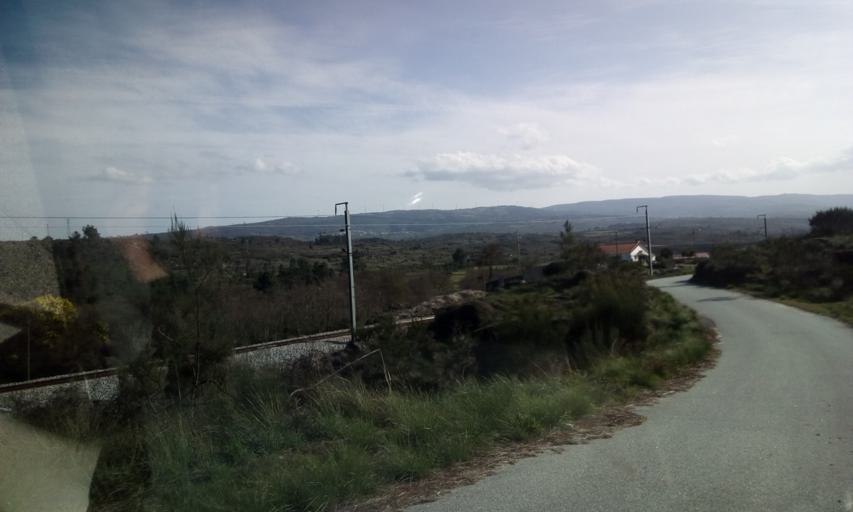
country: PT
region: Guarda
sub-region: Celorico da Beira
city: Celorico da Beira
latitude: 40.6413
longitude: -7.4313
